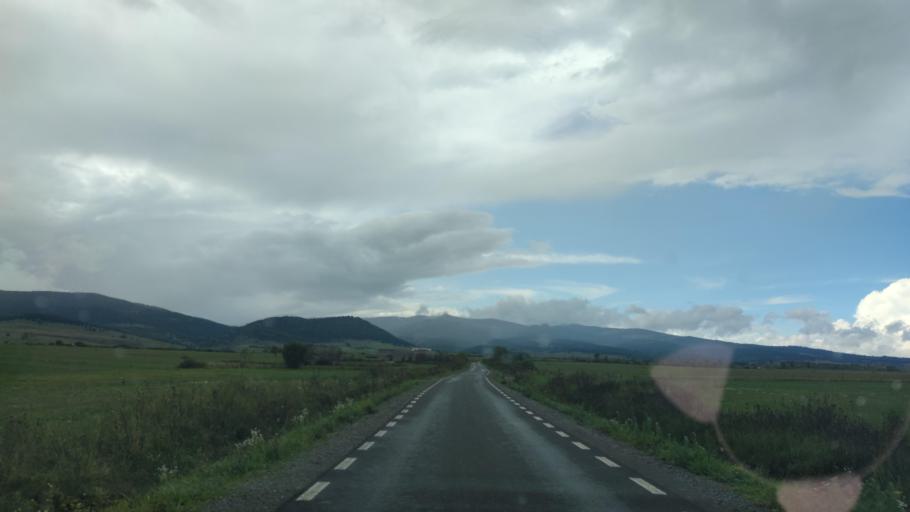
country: RO
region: Harghita
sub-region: Comuna Remetea
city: Remetea
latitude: 46.8074
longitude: 25.4132
